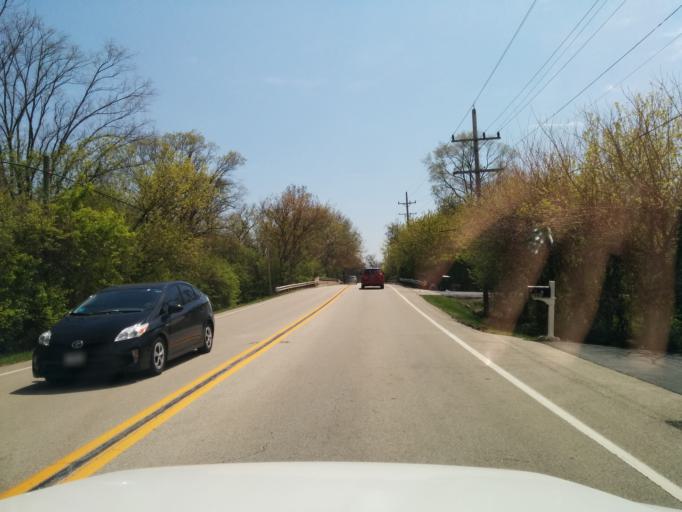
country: US
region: Illinois
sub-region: DuPage County
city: Burr Ridge
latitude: 41.7453
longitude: -87.8961
